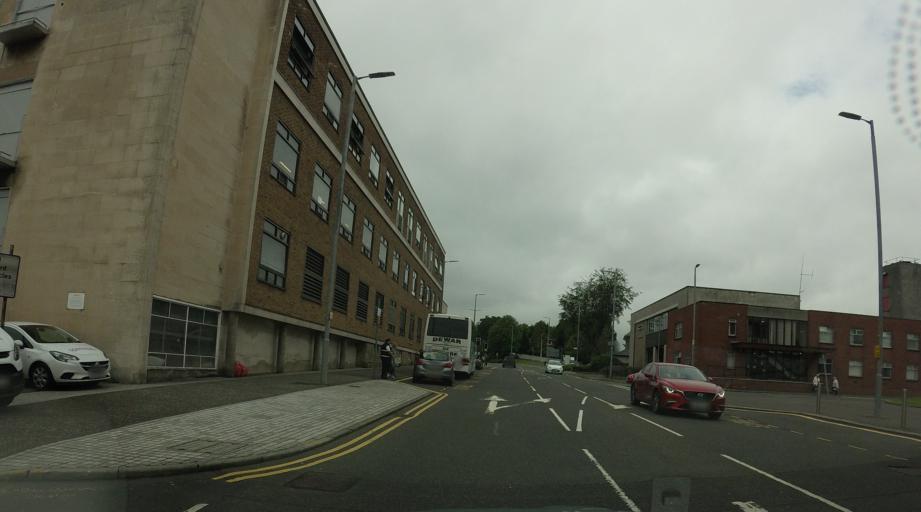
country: GB
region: Scotland
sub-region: South Lanarkshire
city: East Kilbride
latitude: 55.7617
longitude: -4.1755
